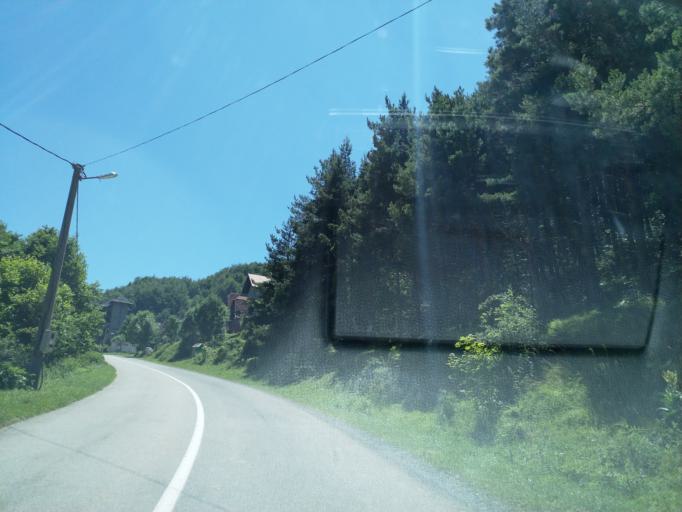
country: XK
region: Mitrovica
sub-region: Komuna e Leposaviqit
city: Leposaviq
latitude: 43.2950
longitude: 20.8794
